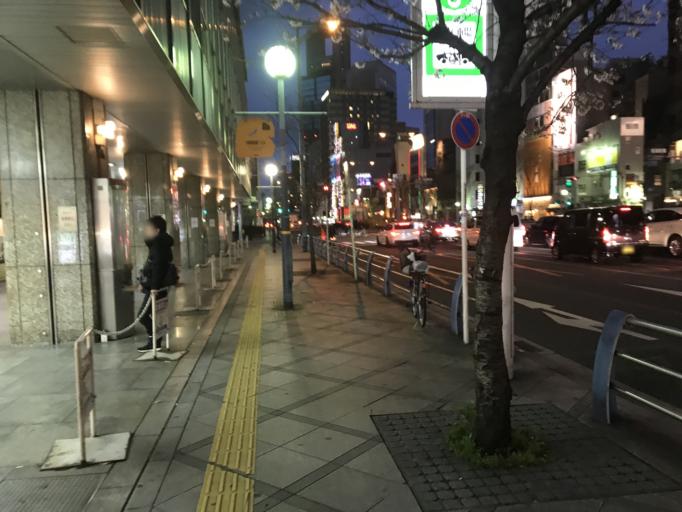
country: JP
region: Osaka
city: Osaka-shi
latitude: 34.6983
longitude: 135.4965
